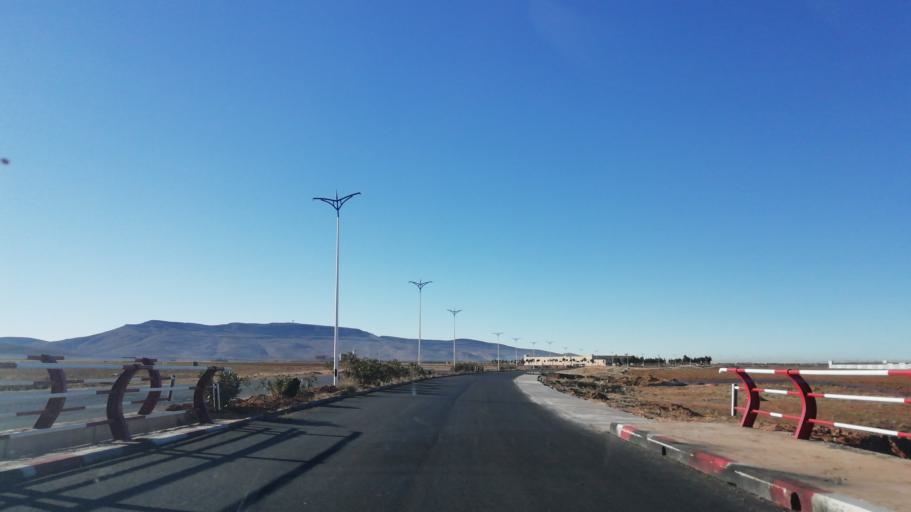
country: DZ
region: El Bayadh
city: El Bayadh
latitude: 33.6951
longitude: 1.0805
